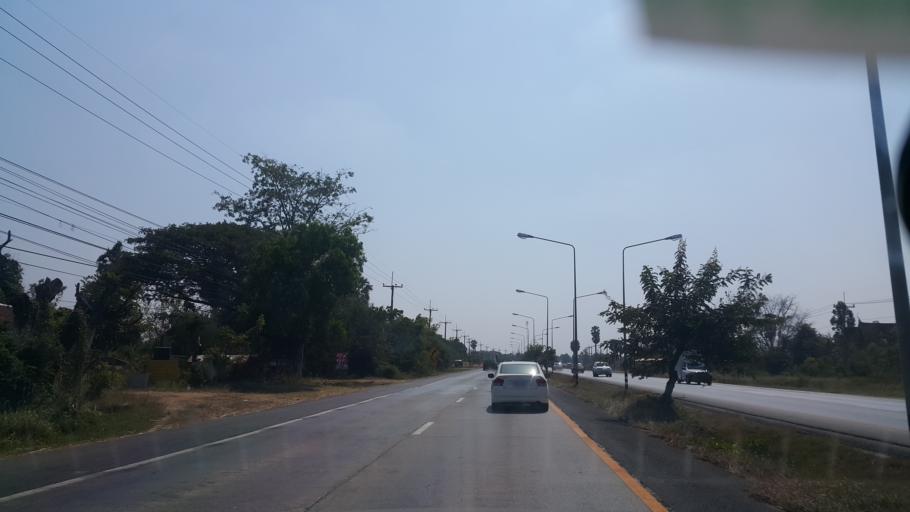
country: TH
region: Nakhon Ratchasima
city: Sida
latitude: 15.5272
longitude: 102.5431
